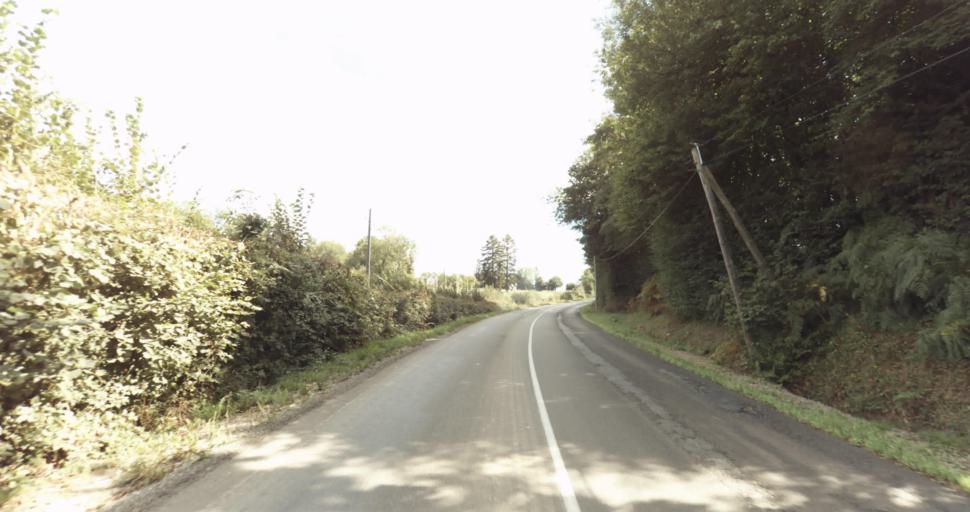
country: FR
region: Lower Normandy
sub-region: Departement de l'Orne
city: Vimoutiers
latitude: 48.9039
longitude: 0.2871
